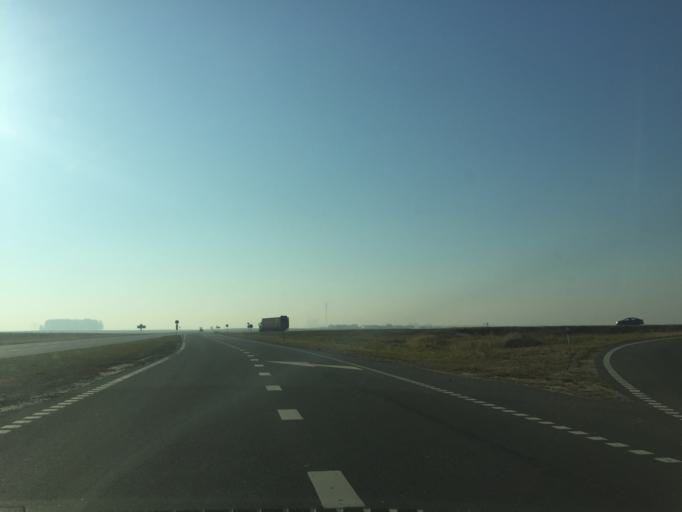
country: BY
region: Gomel
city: Kastsyukowka
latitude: 52.4890
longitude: 30.8186
